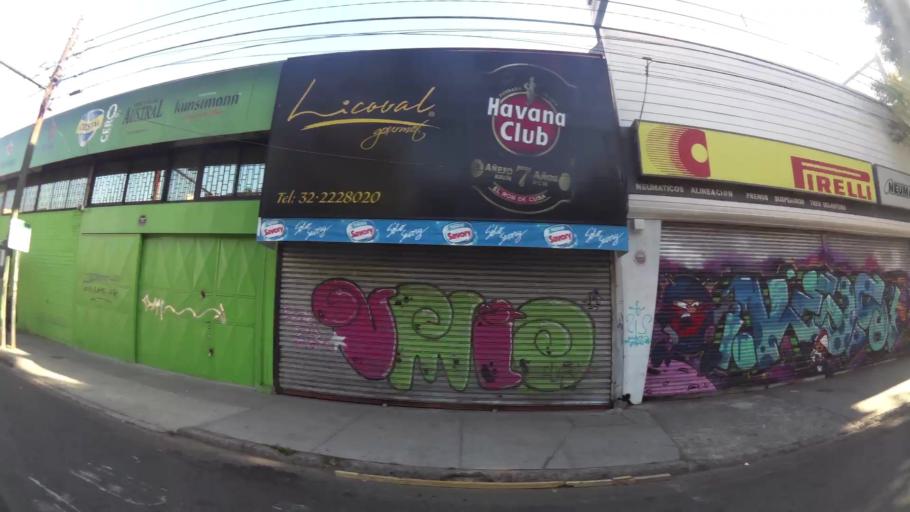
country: CL
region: Valparaiso
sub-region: Provincia de Valparaiso
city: Valparaiso
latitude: -33.0512
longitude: -71.6055
